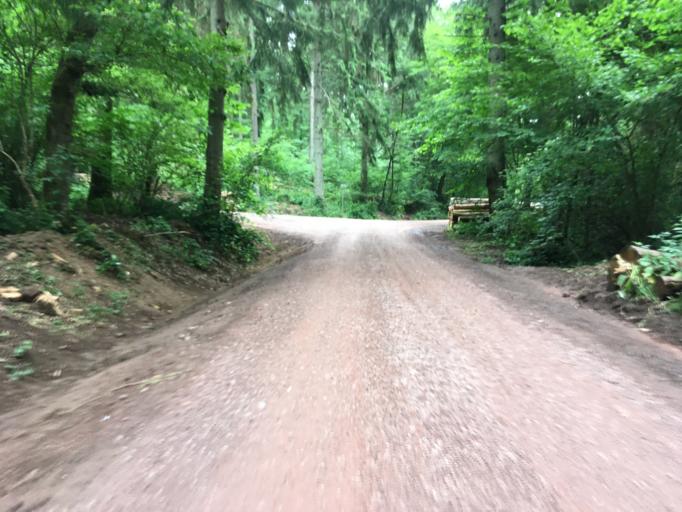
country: DE
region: Saarland
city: Britten
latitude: 49.5108
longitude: 6.6945
